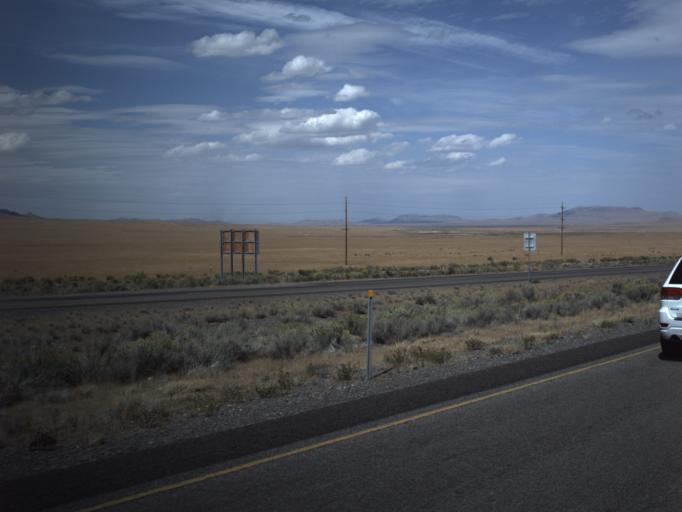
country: US
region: Utah
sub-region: Tooele County
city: Grantsville
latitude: 40.7721
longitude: -112.9786
